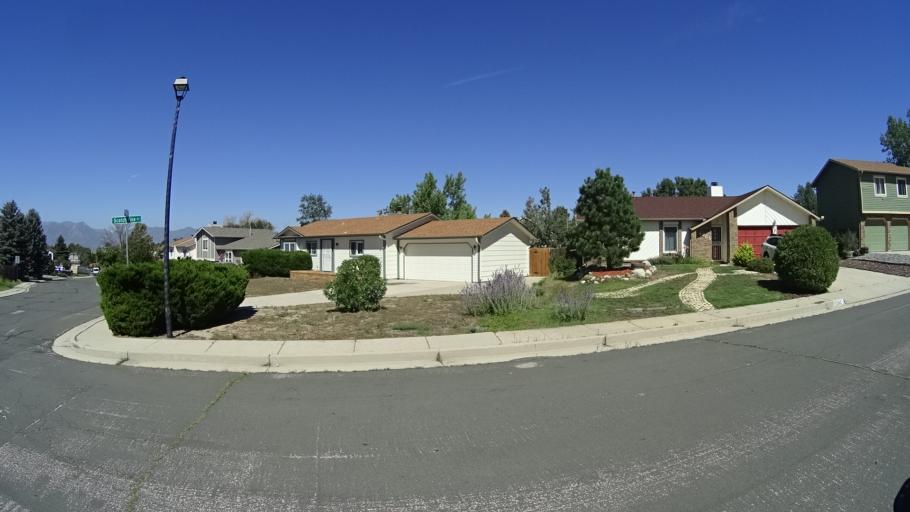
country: US
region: Colorado
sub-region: El Paso County
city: Black Forest
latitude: 38.9463
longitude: -104.7505
